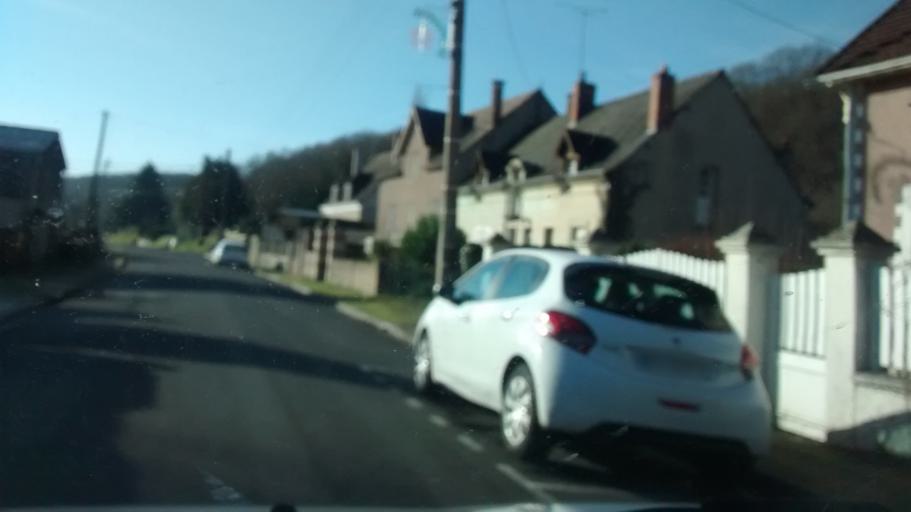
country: FR
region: Centre
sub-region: Departement d'Indre-et-Loire
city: Reugny
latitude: 47.4792
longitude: 0.8828
